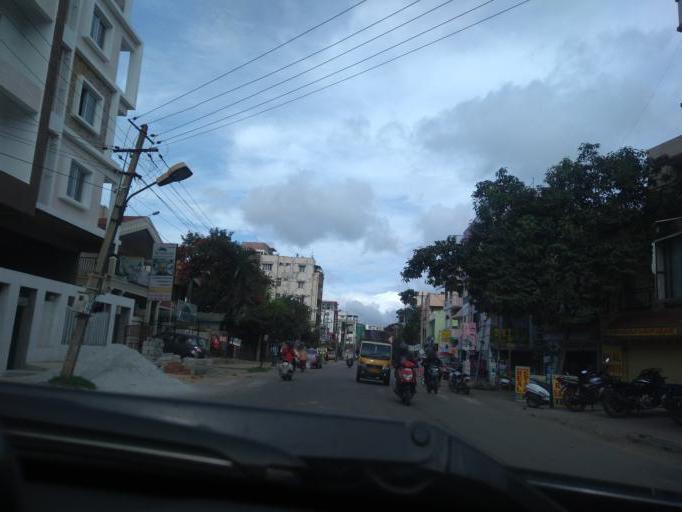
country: IN
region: Karnataka
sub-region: Bangalore Urban
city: Bangalore
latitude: 13.0090
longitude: 77.6560
